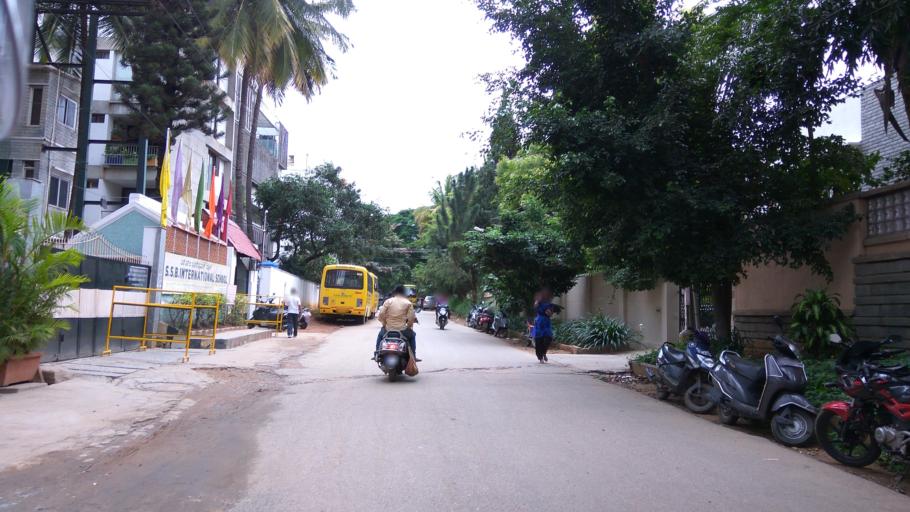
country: IN
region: Karnataka
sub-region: Bangalore Urban
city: Bangalore
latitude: 12.9735
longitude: 77.6403
